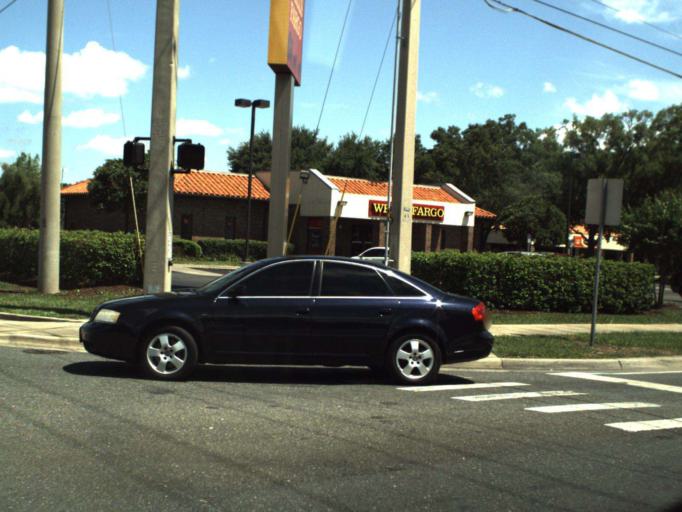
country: US
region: Florida
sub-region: Marion County
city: Ocala
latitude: 29.2005
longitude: -82.1033
